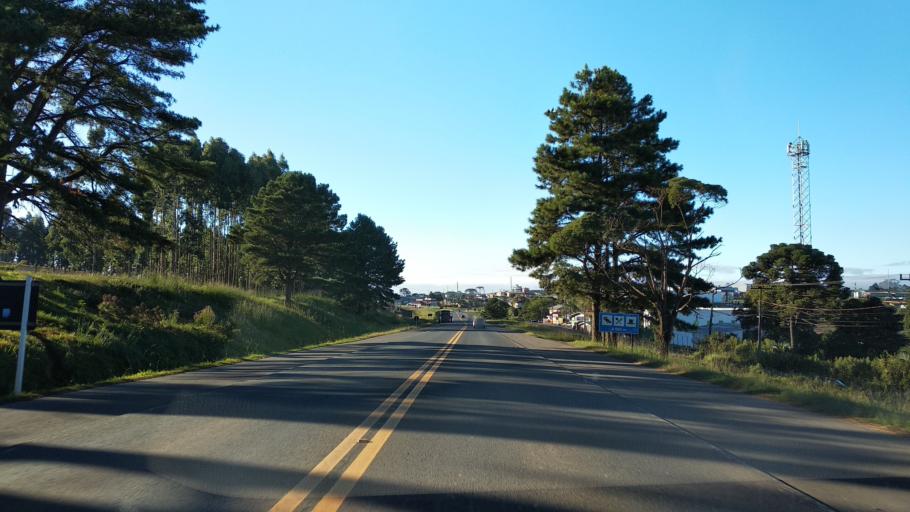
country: BR
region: Santa Catarina
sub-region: Lages
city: Lages
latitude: -27.7970
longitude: -50.3676
